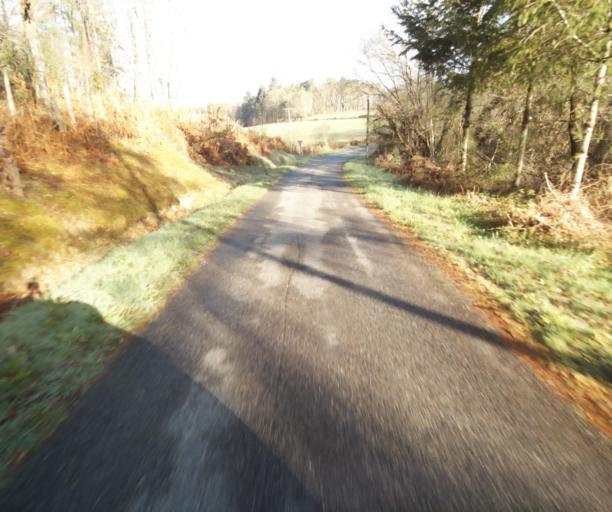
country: FR
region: Limousin
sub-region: Departement de la Correze
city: Correze
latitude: 45.2874
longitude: 1.8642
